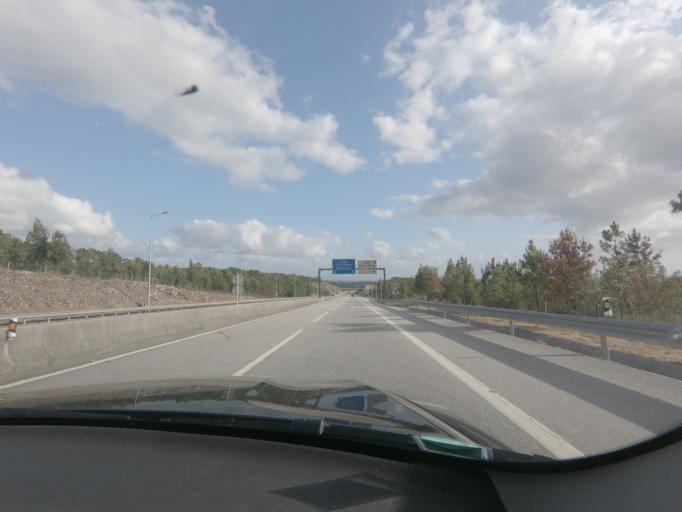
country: PT
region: Viseu
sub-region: Viseu
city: Abraveses
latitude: 40.6816
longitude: -7.9681
